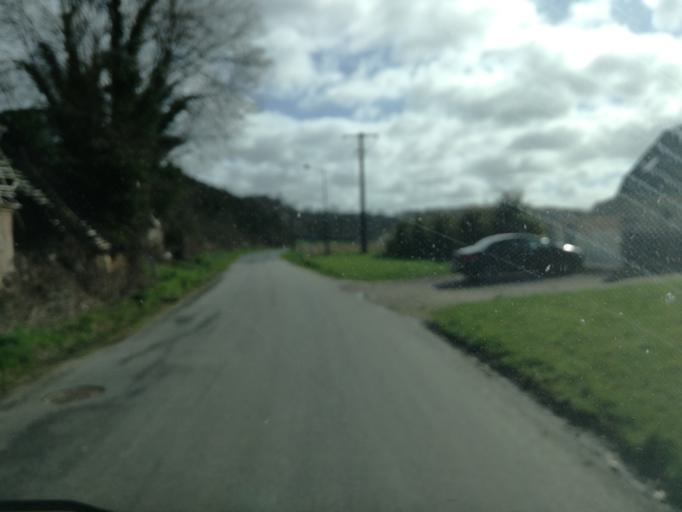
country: FR
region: Haute-Normandie
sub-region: Departement de la Seine-Maritime
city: Bretteville-du-Grand-Caux
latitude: 49.6939
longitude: 0.4784
